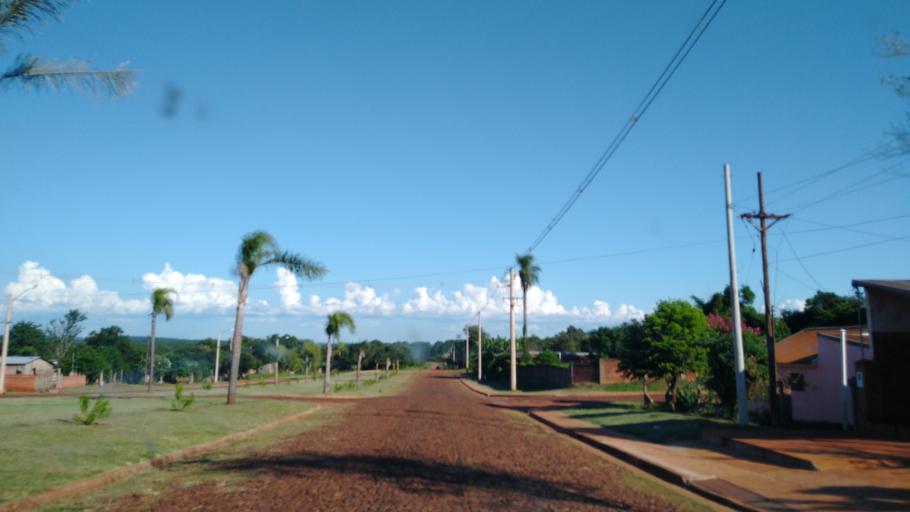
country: AR
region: Misiones
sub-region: Departamento de San Ignacio
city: San Ignacio
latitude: -27.2501
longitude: -55.5295
